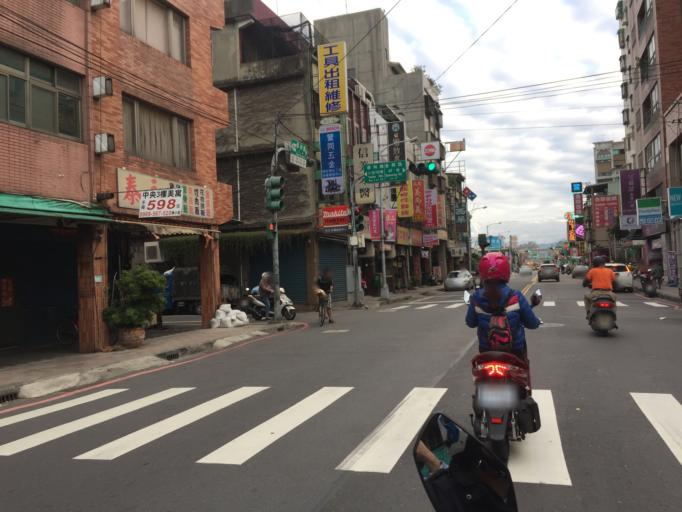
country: TW
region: Taipei
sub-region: Taipei
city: Banqiao
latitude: 25.0595
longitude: 121.4345
